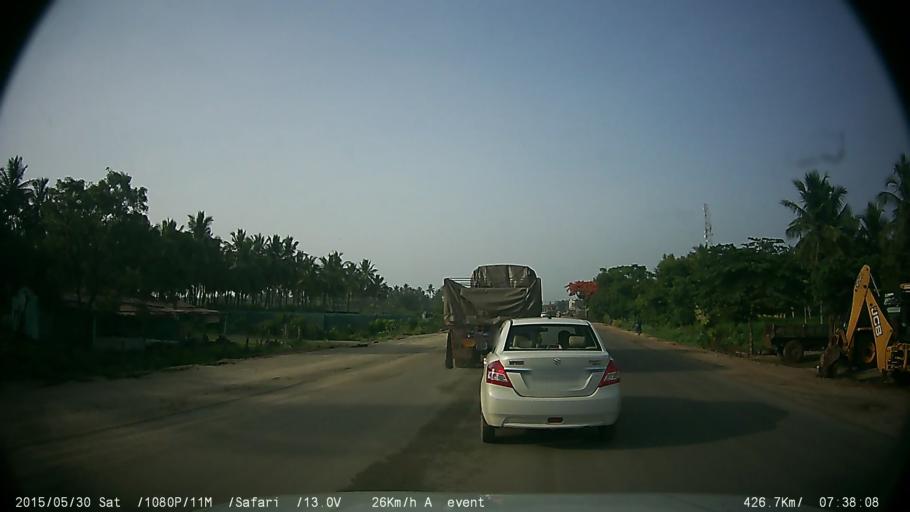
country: IN
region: Karnataka
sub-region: Chamrajnagar
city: Gundlupet
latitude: 11.9415
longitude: 76.6706
